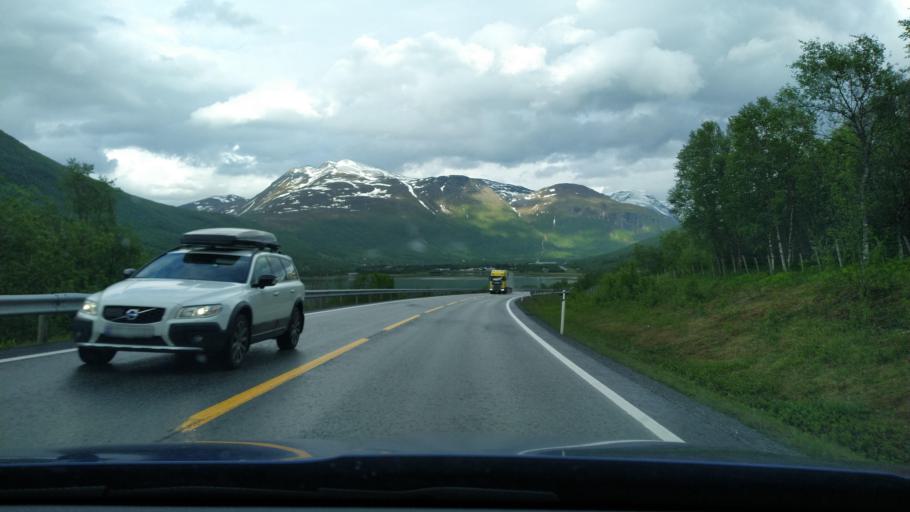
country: NO
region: Troms
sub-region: Balsfjord
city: Storsteinnes
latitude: 69.2153
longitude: 19.4999
